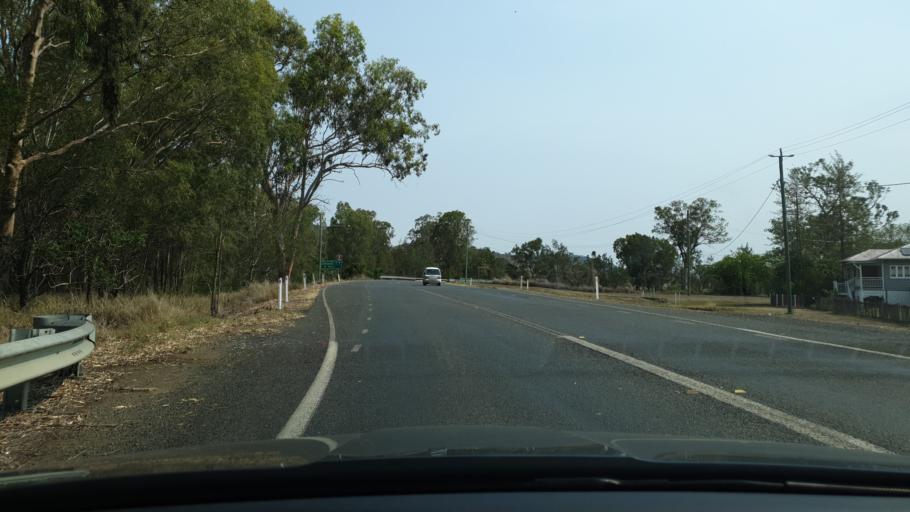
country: AU
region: Queensland
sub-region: Ipswich
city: Deebing Heights
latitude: -28.0061
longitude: 152.6804
